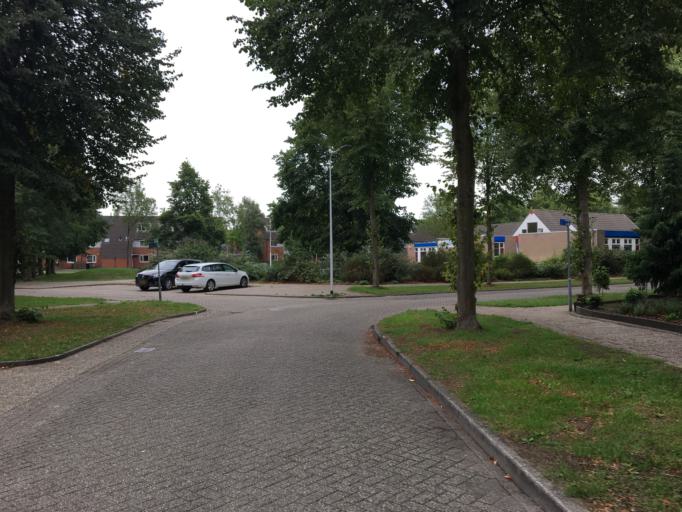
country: NL
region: Utrecht
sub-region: Gemeente Houten
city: Houten
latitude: 52.0418
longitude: 5.1762
